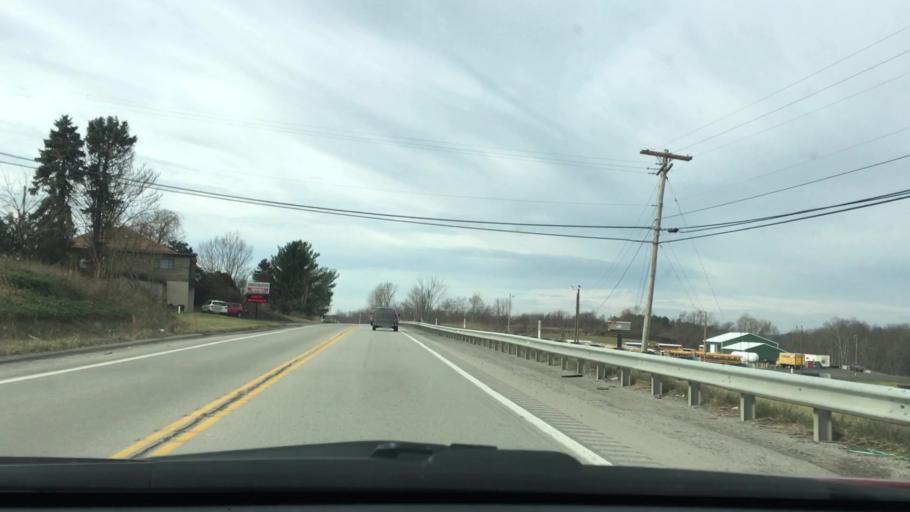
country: US
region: Pennsylvania
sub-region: Fayette County
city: South Uniontown
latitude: 39.8929
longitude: -79.8172
